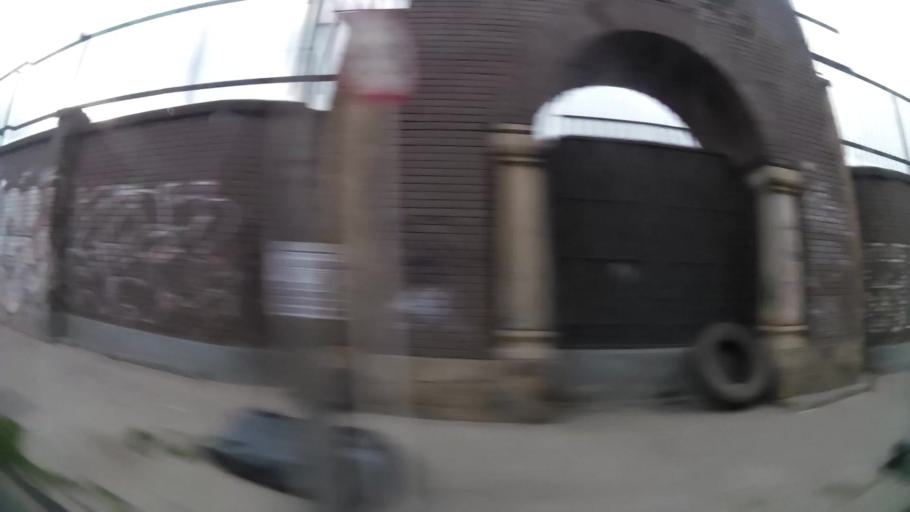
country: CO
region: Bogota D.C.
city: Bogota
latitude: 4.5867
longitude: -74.1230
